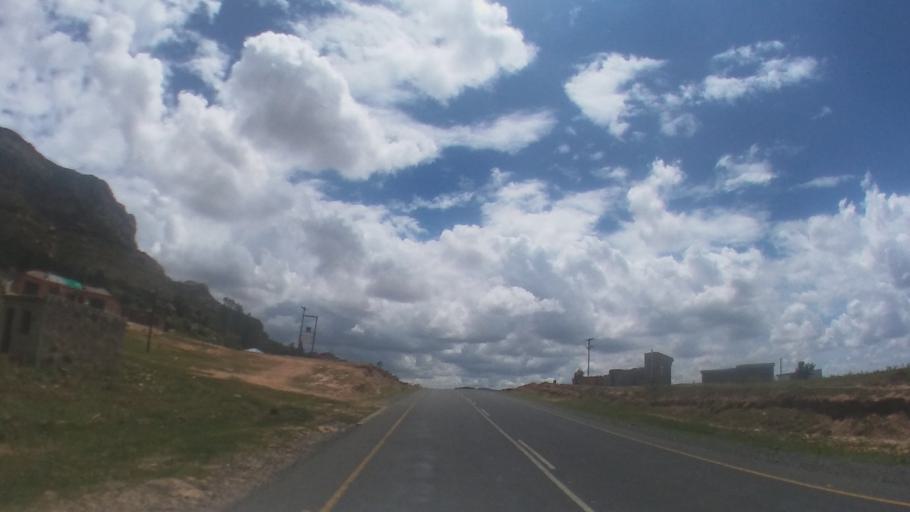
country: LS
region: Maseru
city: Maseru
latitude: -29.4323
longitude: 27.4691
